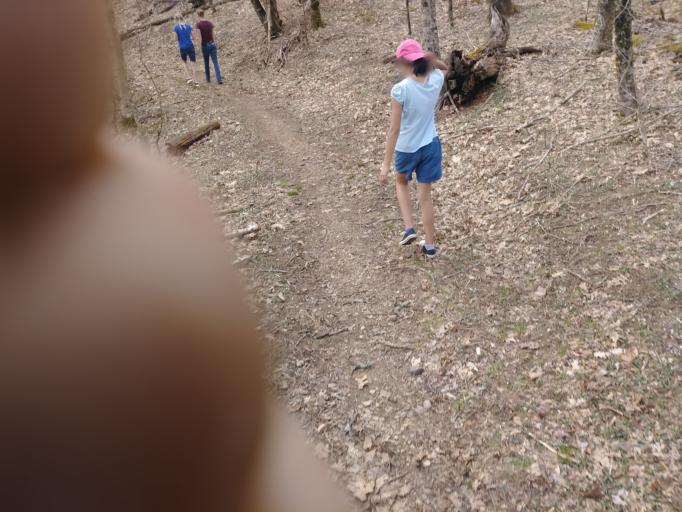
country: US
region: Tennessee
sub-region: Greene County
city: Tusculum
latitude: 36.0530
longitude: -82.6698
